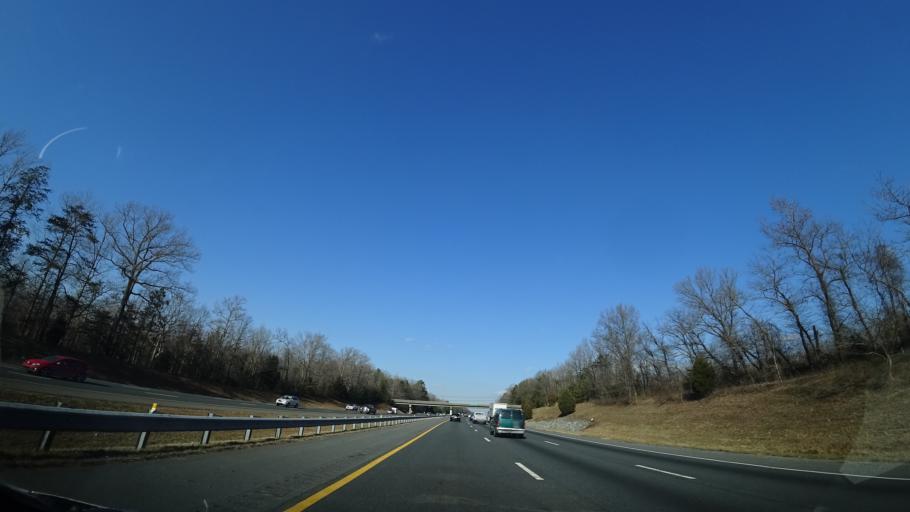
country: US
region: Virginia
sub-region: Spotsylvania County
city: Spotsylvania Courthouse
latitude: 38.0881
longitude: -77.5169
